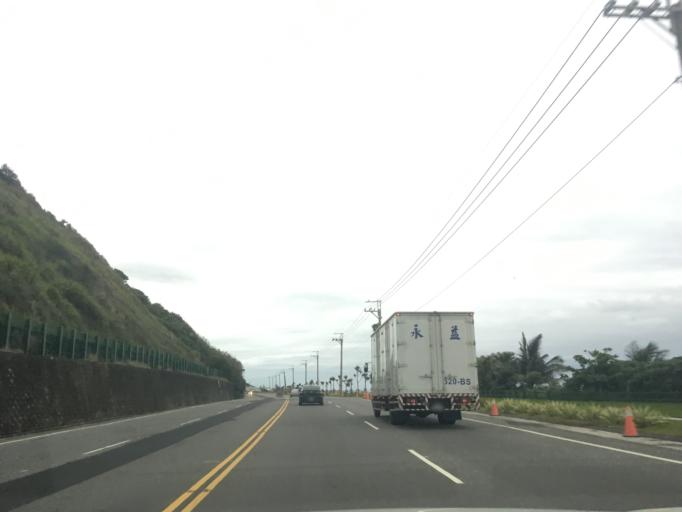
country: TW
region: Taiwan
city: Hengchun
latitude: 22.3444
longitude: 120.8981
